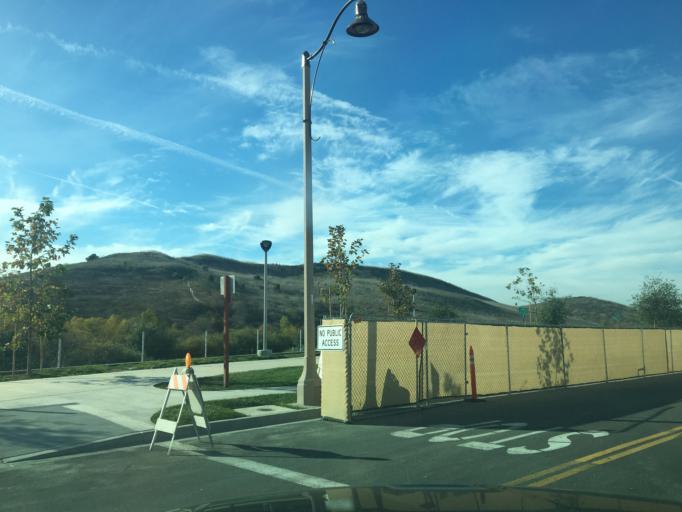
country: US
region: California
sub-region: Orange County
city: Laguna Woods
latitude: 33.6384
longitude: -117.7480
